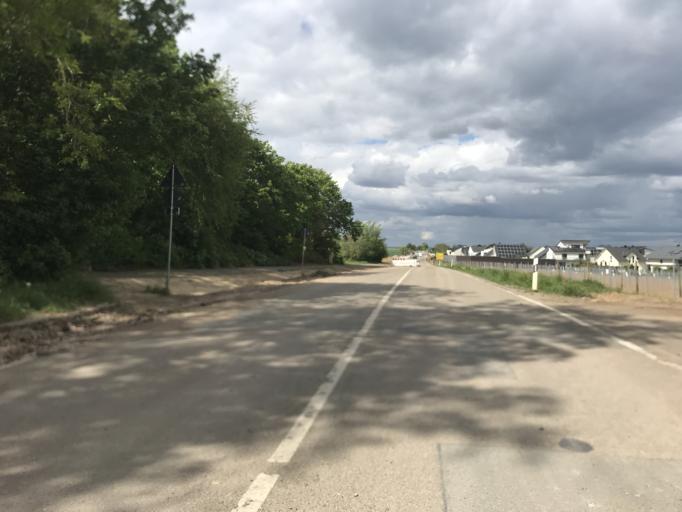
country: DE
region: Rheinland-Pfalz
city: Harxheim
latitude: 49.9098
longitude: 8.2690
